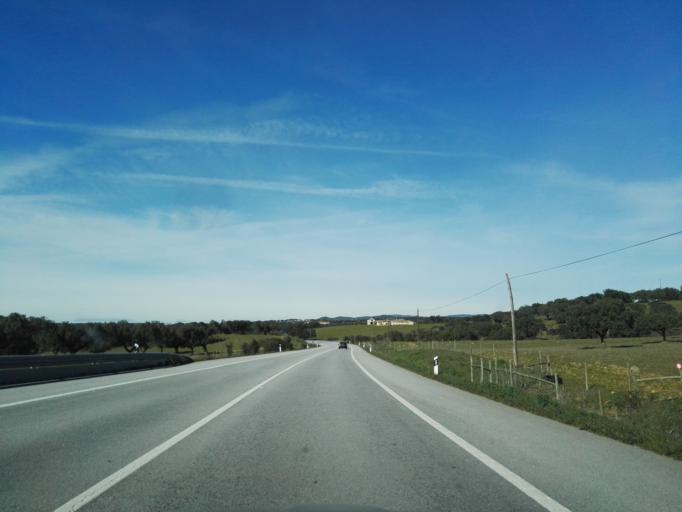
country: PT
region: Portalegre
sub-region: Portalegre
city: Alegrete
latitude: 39.1769
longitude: -7.3403
